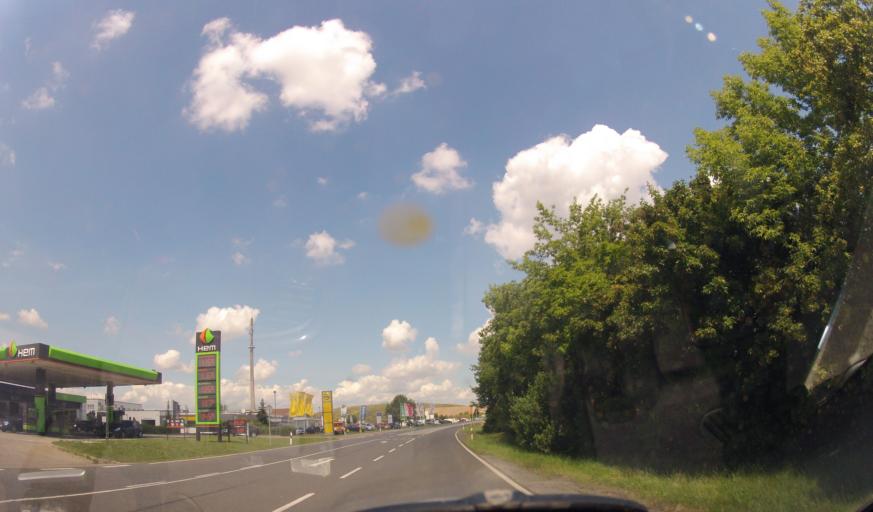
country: DE
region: Saxony
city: Zinna
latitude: 51.5555
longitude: 12.9664
